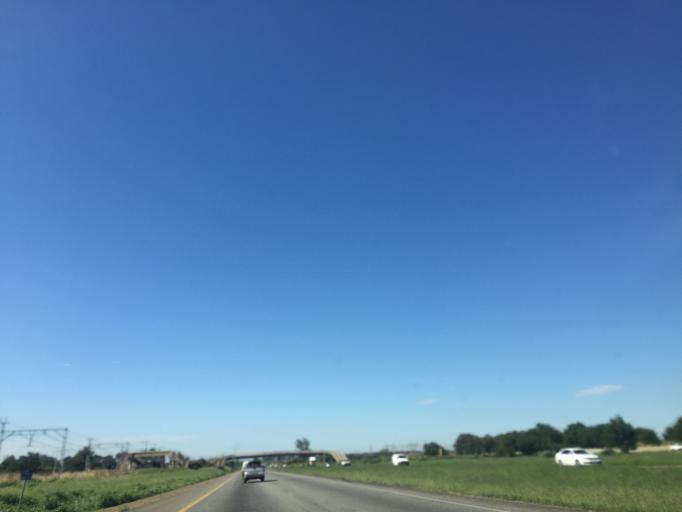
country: ZA
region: Gauteng
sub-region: Sedibeng District Municipality
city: Meyerton
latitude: -26.5841
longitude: 27.9950
